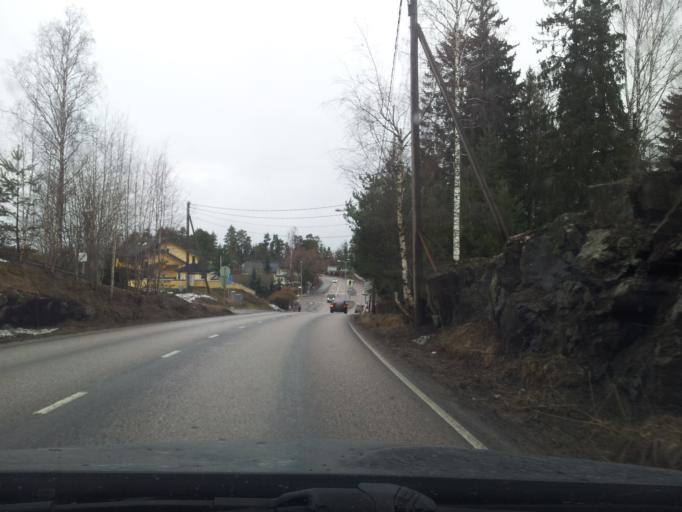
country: FI
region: Uusimaa
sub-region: Helsinki
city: Espoo
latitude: 60.1713
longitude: 24.6890
